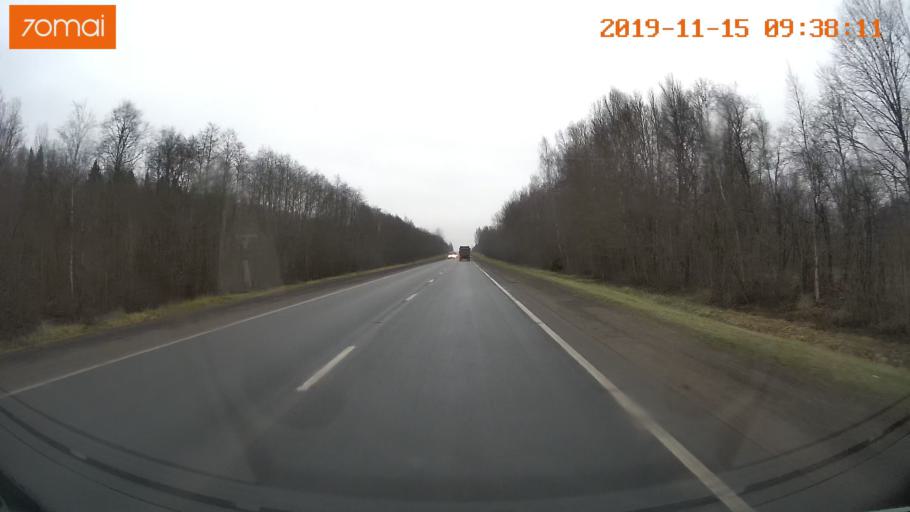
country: RU
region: Vologda
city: Sheksna
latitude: 59.2343
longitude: 38.4506
